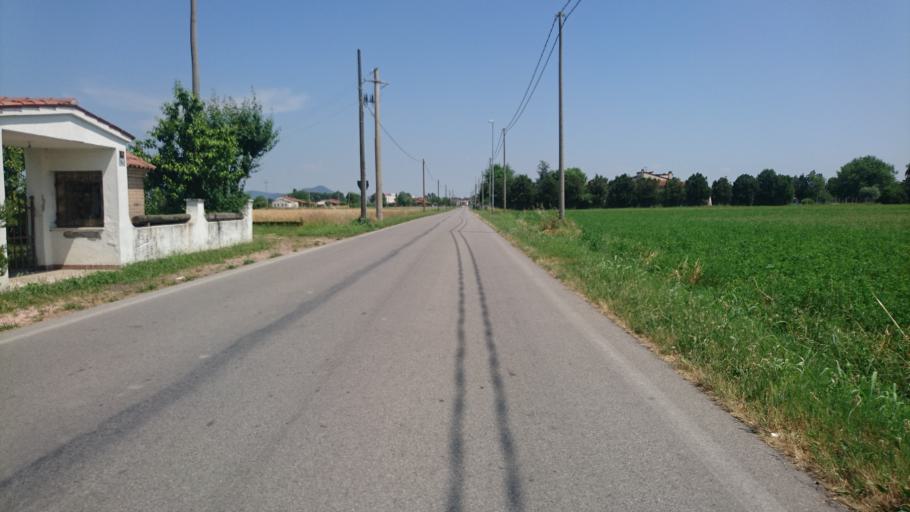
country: IT
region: Veneto
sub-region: Provincia di Padova
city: Solesino
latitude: 45.1653
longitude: 11.7366
